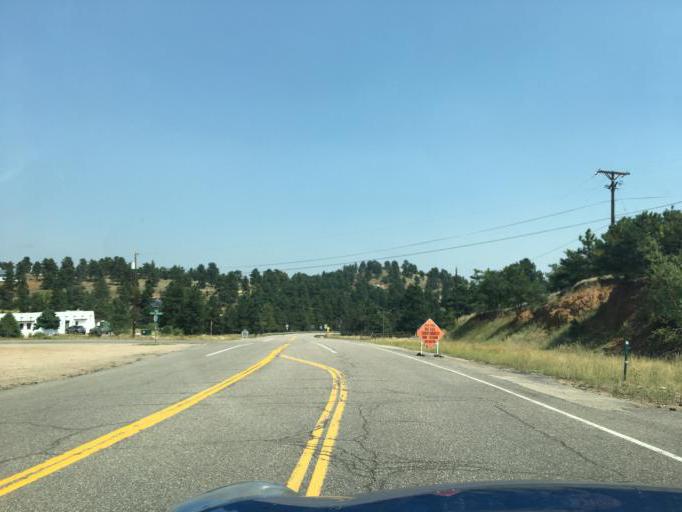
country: US
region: Colorado
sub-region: Jefferson County
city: Genesee
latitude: 39.7104
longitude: -105.2726
